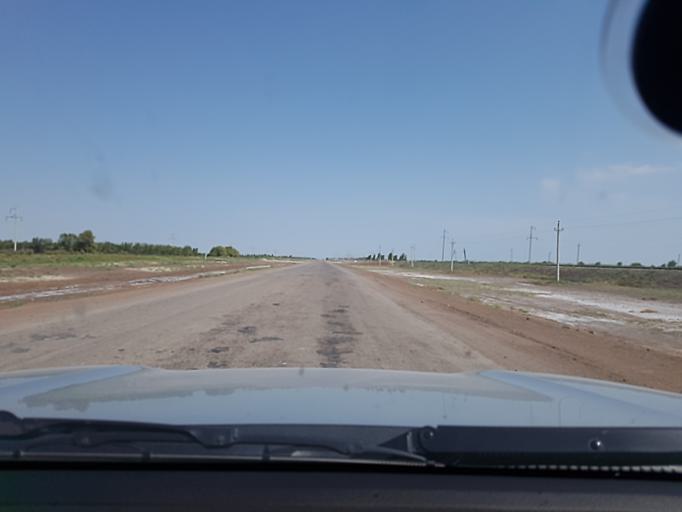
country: UZ
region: Karakalpakstan
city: Xo'jayli Shahri
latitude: 42.2595
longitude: 59.3354
